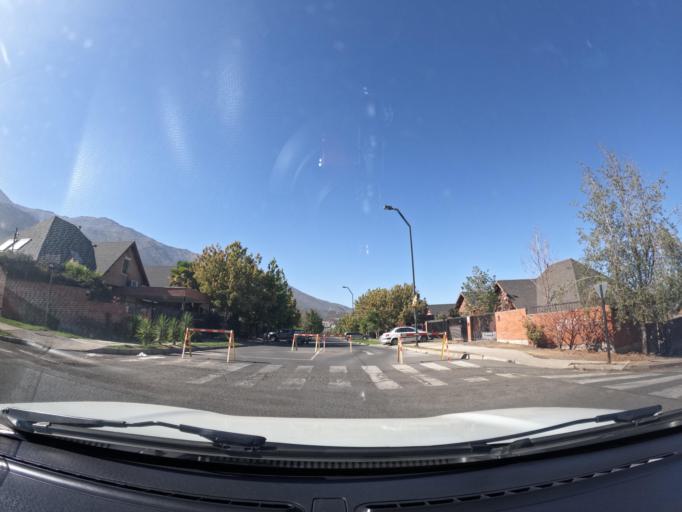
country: CL
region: Santiago Metropolitan
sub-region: Provincia de Santiago
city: Villa Presidente Frei, Nunoa, Santiago, Chile
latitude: -33.5042
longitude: -70.5269
